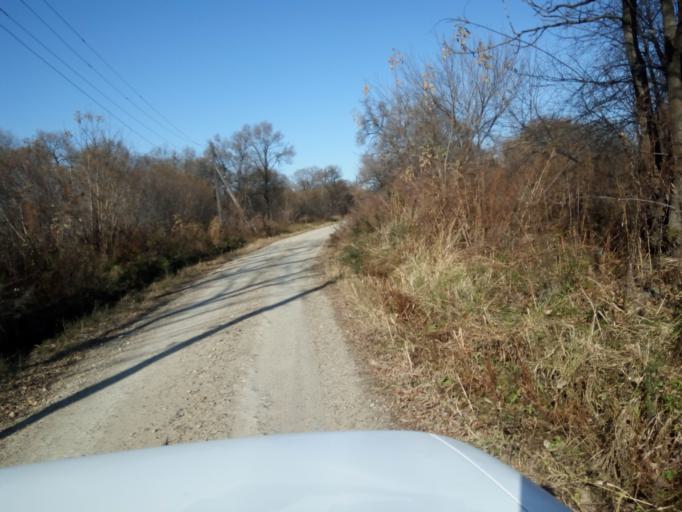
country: RU
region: Primorskiy
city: Lazo
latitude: 45.8805
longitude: 133.6435
